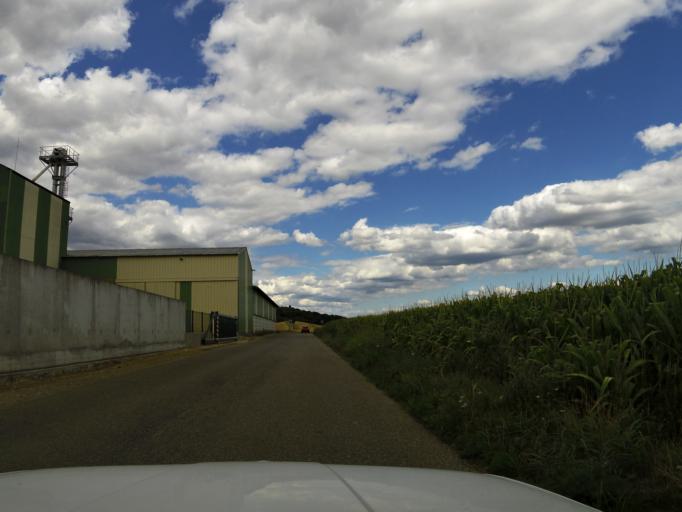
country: FR
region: Rhone-Alpes
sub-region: Departement de l'Ain
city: Meximieux
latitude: 45.8969
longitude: 5.2034
